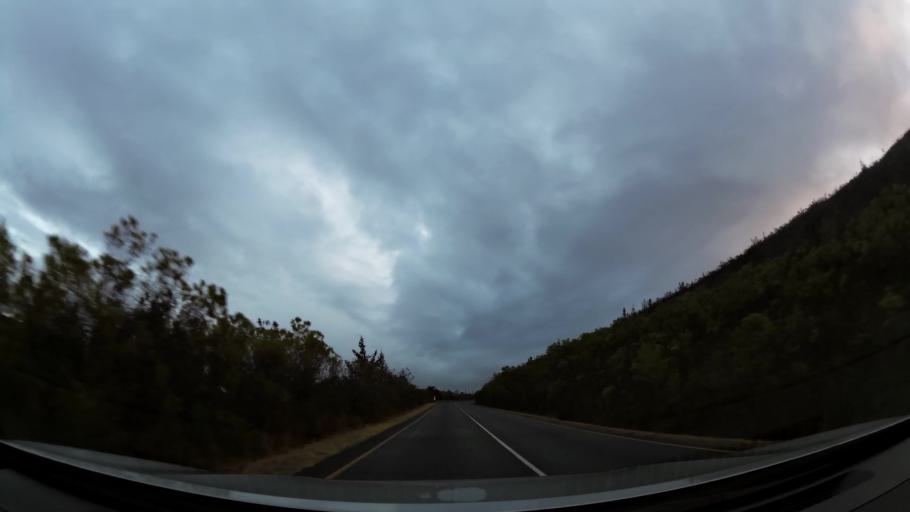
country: ZA
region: Western Cape
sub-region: Overberg District Municipality
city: Swellendam
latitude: -33.9869
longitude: 20.7125
